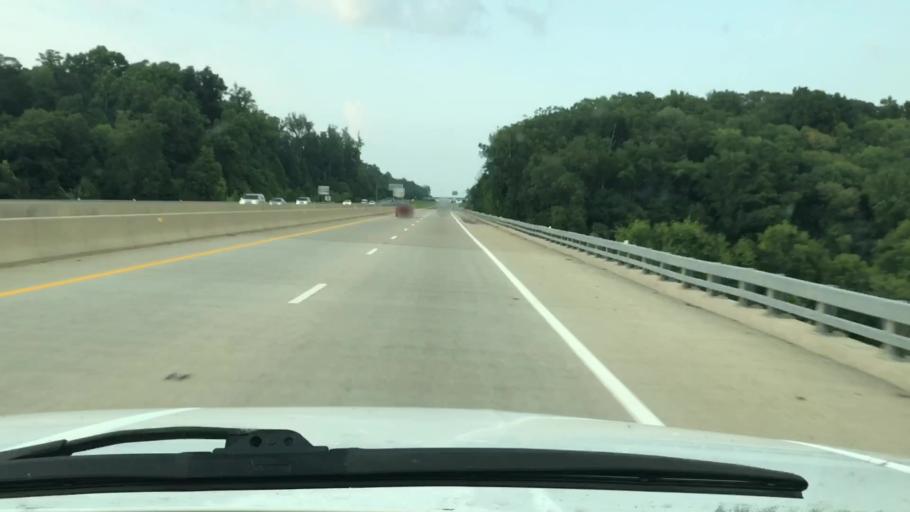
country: US
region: Virginia
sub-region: Henrico County
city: Short Pump
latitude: 37.5765
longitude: -77.6788
